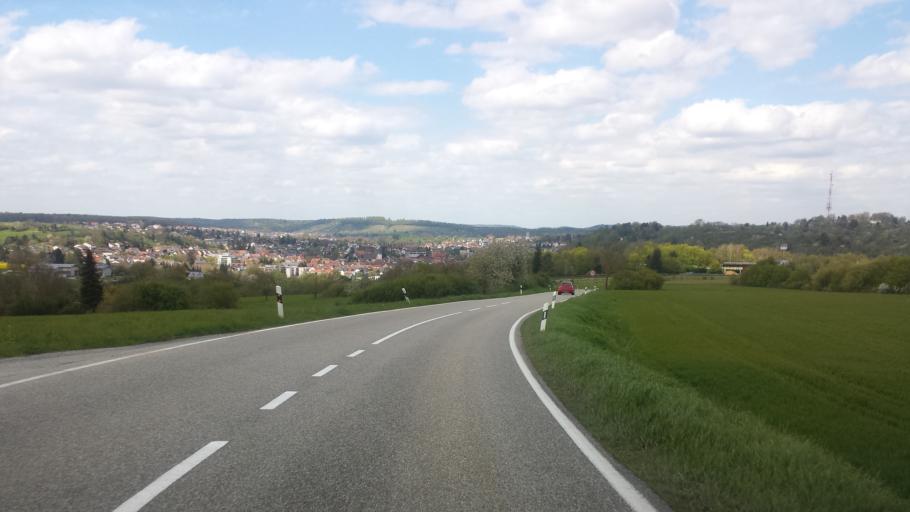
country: DE
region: Baden-Wuerttemberg
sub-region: Karlsruhe Region
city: Muhlacker
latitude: 48.9265
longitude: 8.8441
